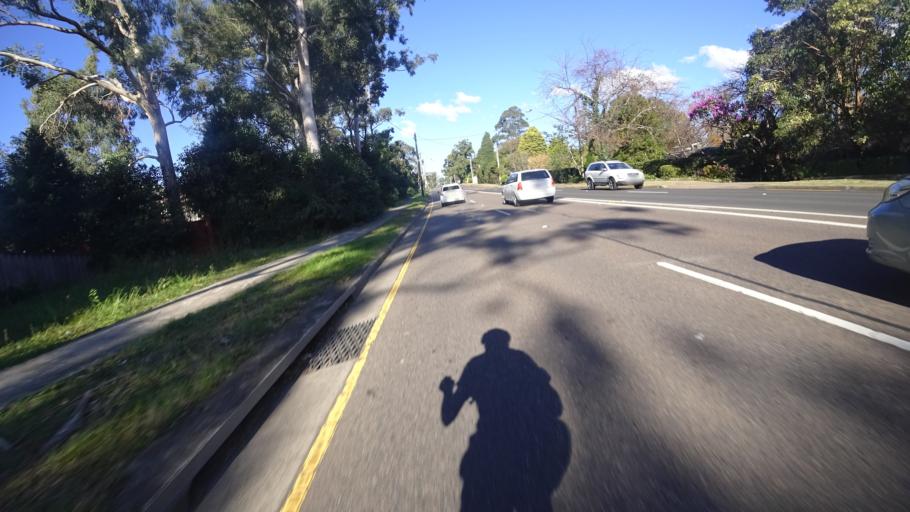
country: AU
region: New South Wales
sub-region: The Hills Shire
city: West Pennant
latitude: -33.7339
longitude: 151.0285
